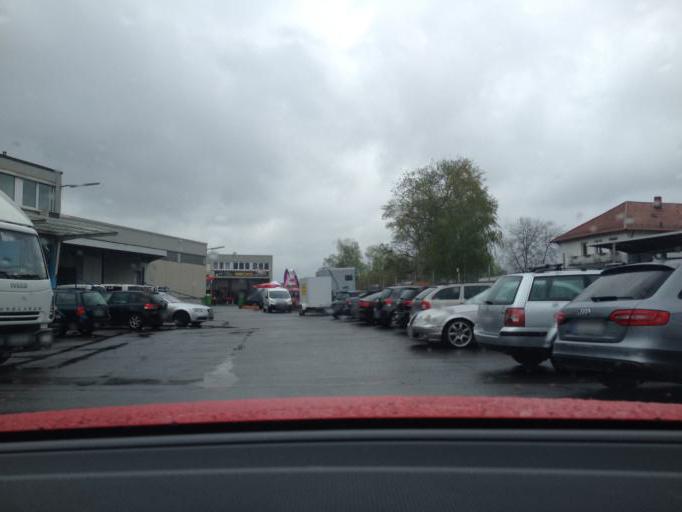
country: DE
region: Bavaria
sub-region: Upper Franconia
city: Bamberg
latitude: 49.9060
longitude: 10.8792
